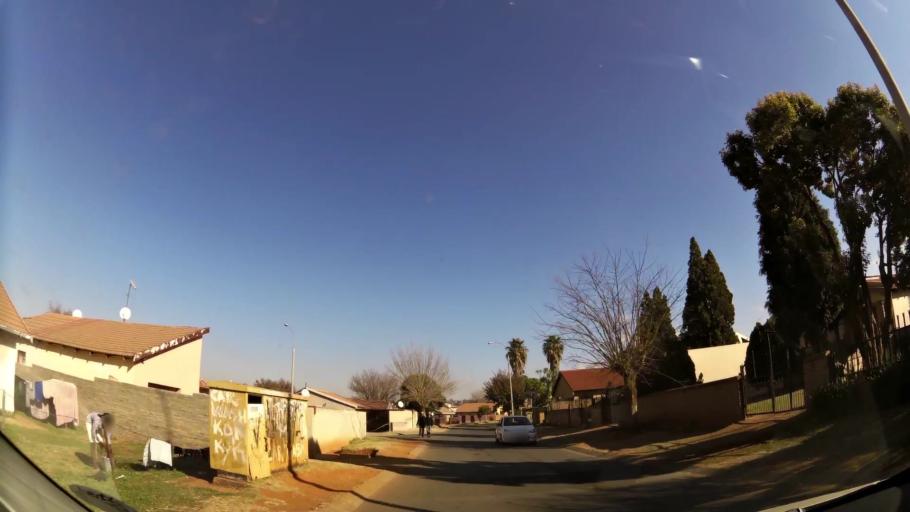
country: ZA
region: Gauteng
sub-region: City of Johannesburg Metropolitan Municipality
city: Roodepoort
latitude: -26.1582
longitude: 27.8473
